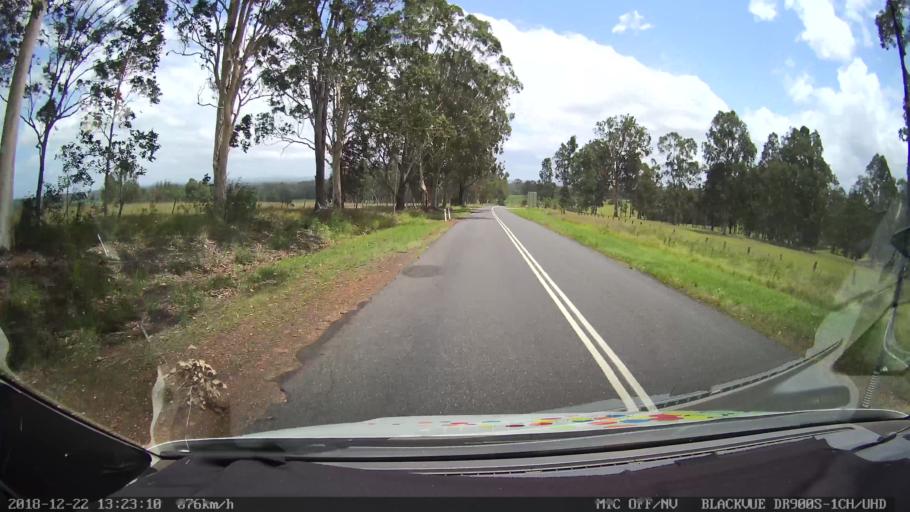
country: AU
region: New South Wales
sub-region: Clarence Valley
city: Coutts Crossing
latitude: -29.7952
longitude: 152.9093
